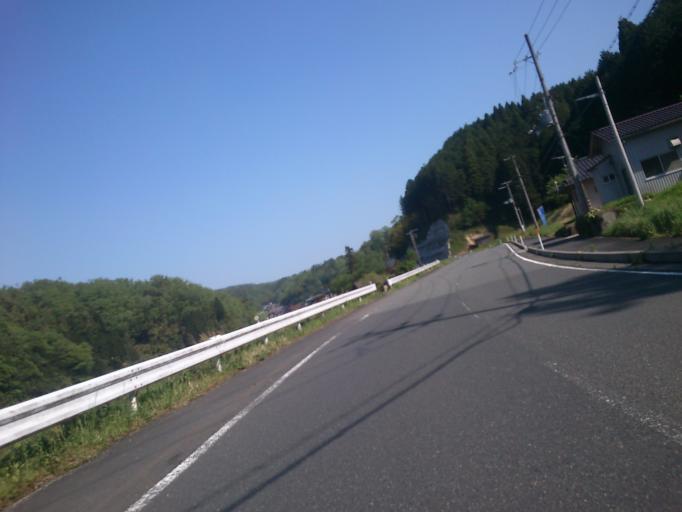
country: JP
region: Kyoto
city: Miyazu
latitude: 35.6061
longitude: 135.1370
